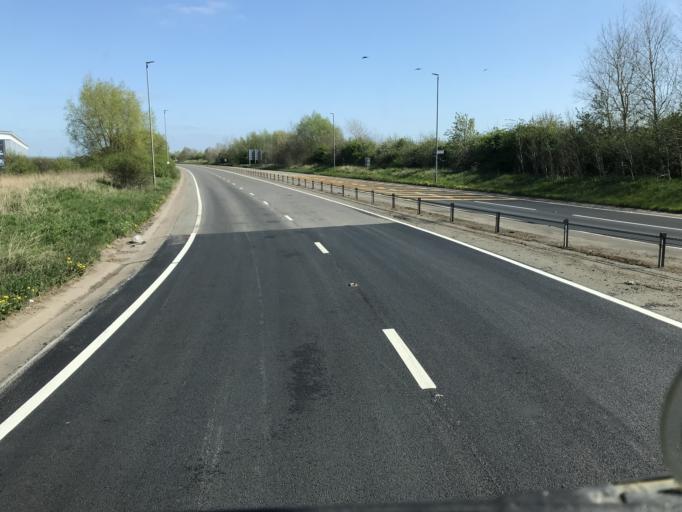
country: GB
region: England
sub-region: Cheshire East
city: Crewe
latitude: 53.0709
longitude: -2.4377
